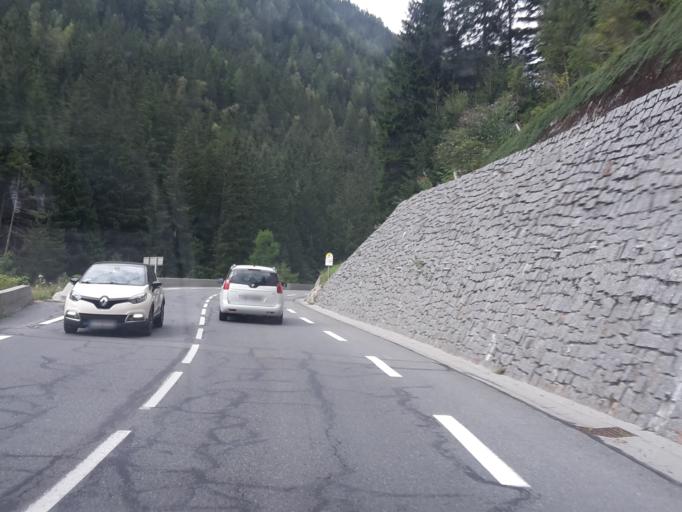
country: FR
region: Rhone-Alpes
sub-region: Departement de la Haute-Savoie
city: Chamonix-Mont-Blanc
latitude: 45.9570
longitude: 6.9030
